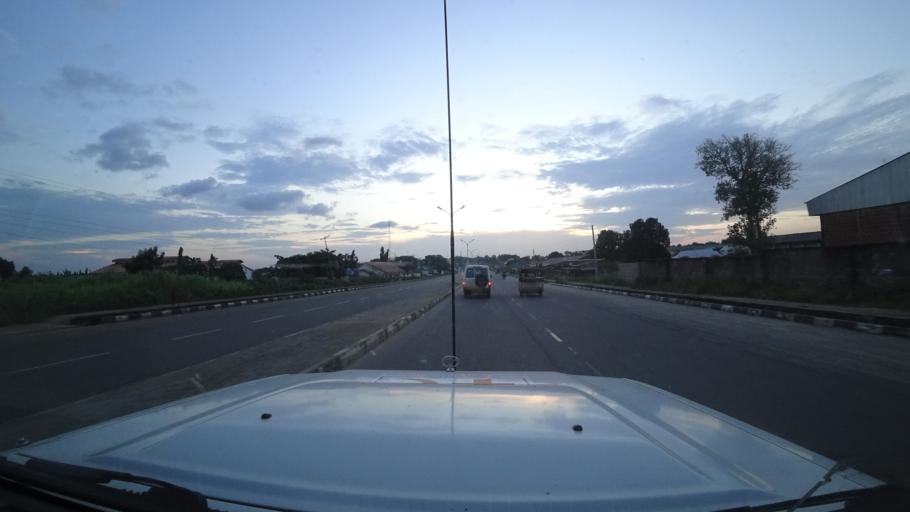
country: NG
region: Niger
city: Minna
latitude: 9.6411
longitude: 6.5479
